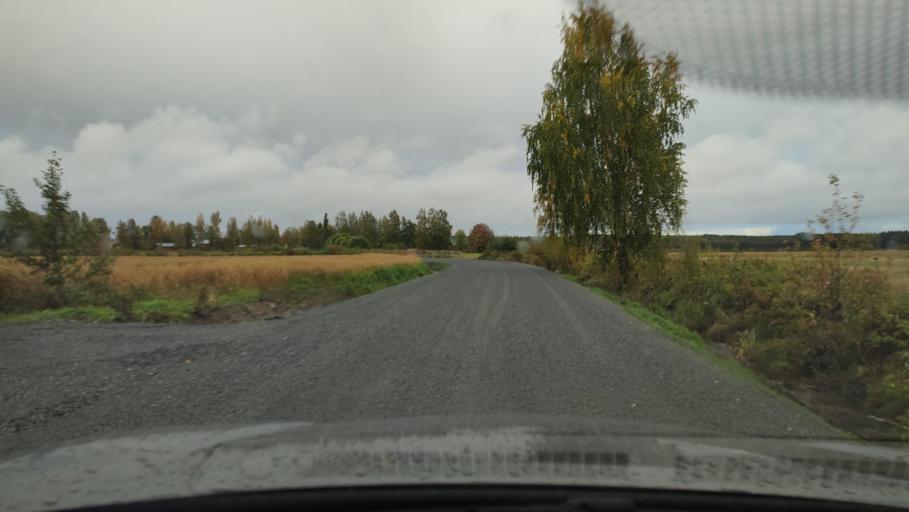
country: FI
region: Southern Ostrobothnia
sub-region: Suupohja
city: Karijoki
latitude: 62.2272
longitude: 21.6258
